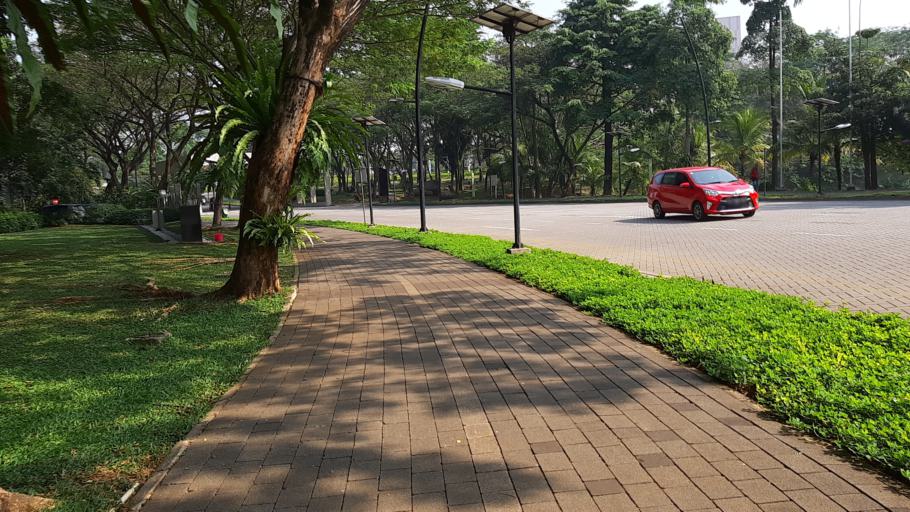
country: ID
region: West Java
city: Serpong
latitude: -6.3007
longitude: 106.6527
